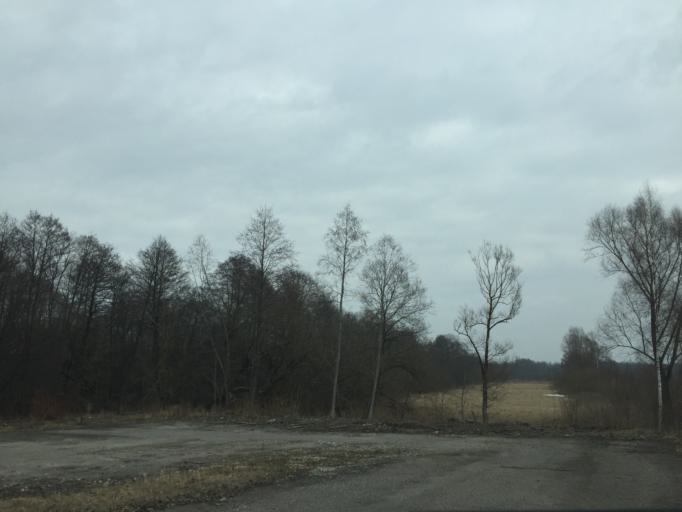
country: LV
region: Kekava
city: Balozi
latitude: 56.7678
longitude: 24.1094
